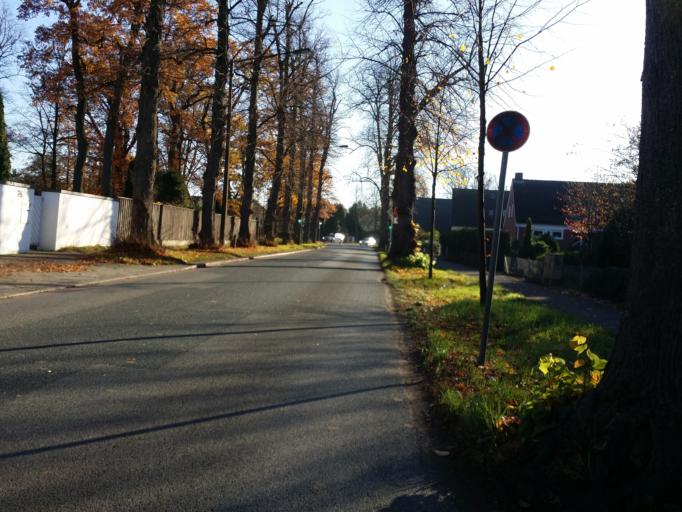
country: DE
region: Lower Saxony
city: Lilienthal
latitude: 53.0810
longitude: 8.9389
